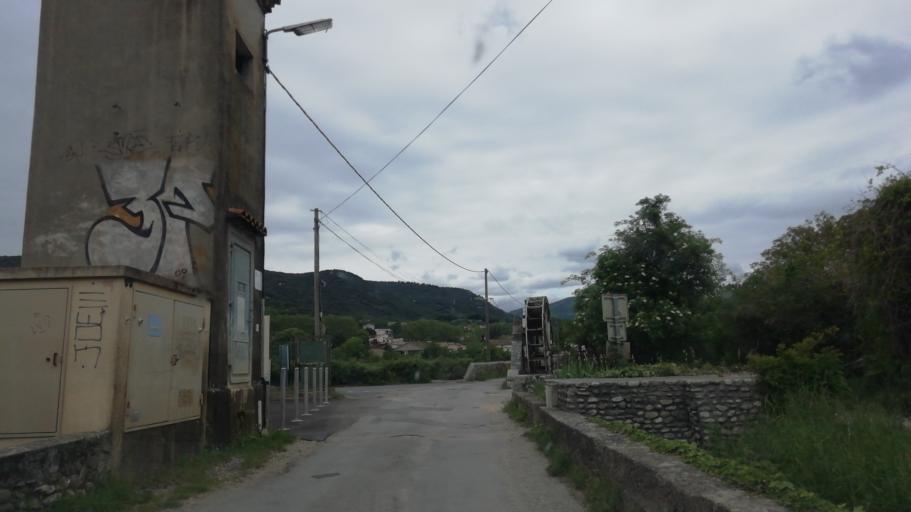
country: FR
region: Languedoc-Roussillon
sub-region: Departement de l'Herault
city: Cazilhac
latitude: 43.9239
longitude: 3.7083
